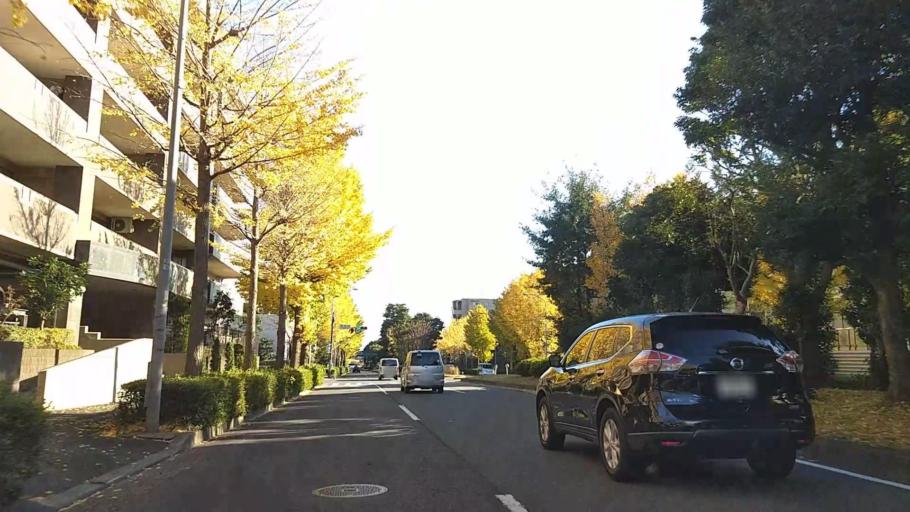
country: JP
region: Tokyo
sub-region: Machida-shi
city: Machida
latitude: 35.5399
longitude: 139.5544
